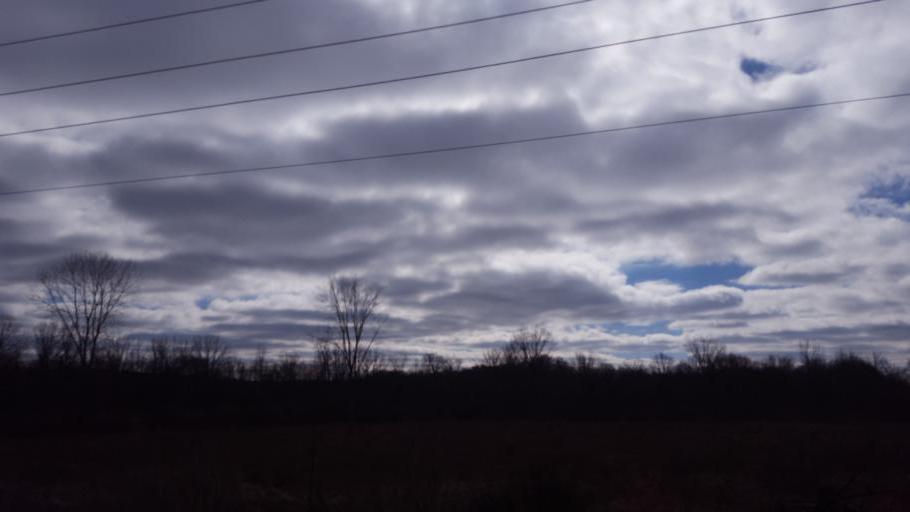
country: US
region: Ohio
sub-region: Sandusky County
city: Bellville
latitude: 40.5573
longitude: -82.4817
